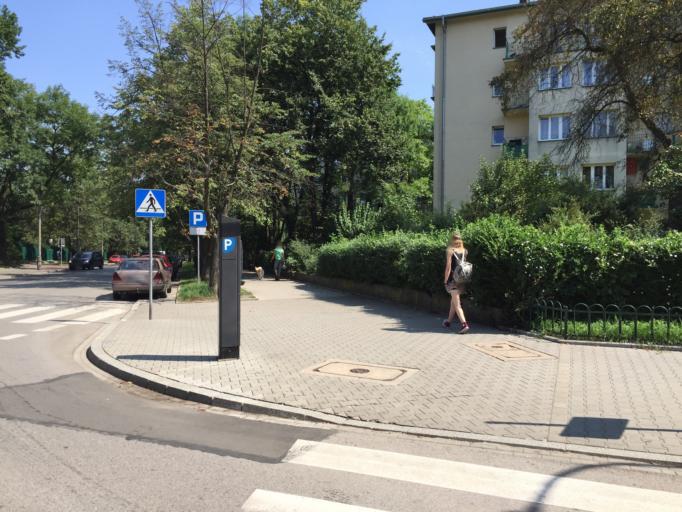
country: PL
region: Lesser Poland Voivodeship
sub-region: Krakow
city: Krakow
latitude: 50.0556
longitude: 19.9221
